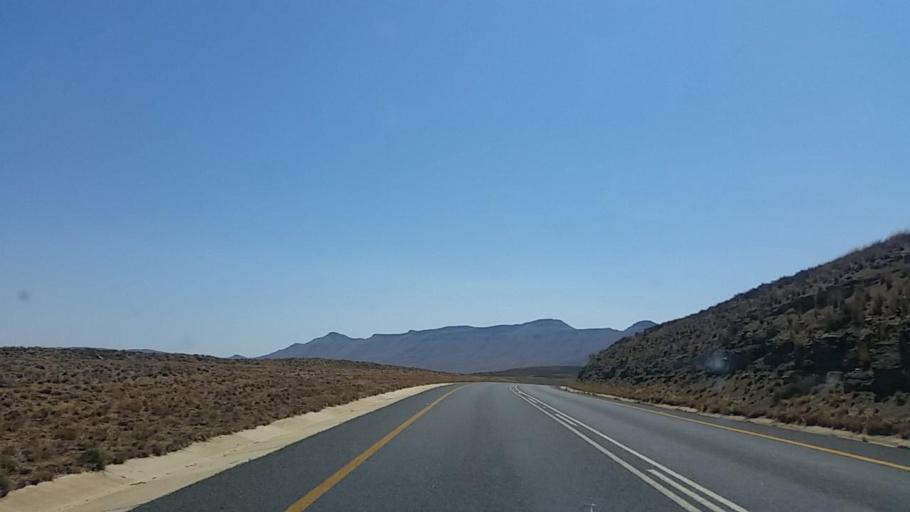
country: ZA
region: Eastern Cape
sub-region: Chris Hani District Municipality
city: Middelburg
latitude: -31.8775
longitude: 24.8235
